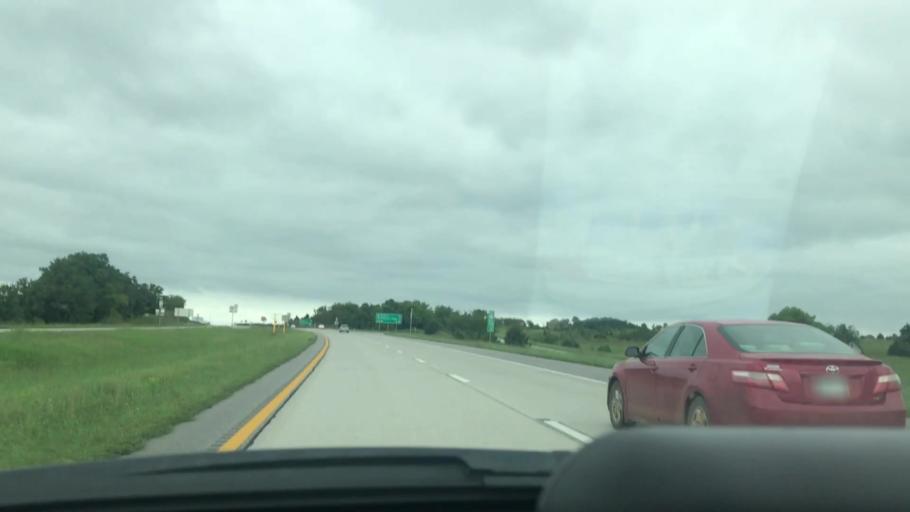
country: US
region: Missouri
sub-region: Greene County
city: Fair Grove
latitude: 37.4564
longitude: -93.1401
